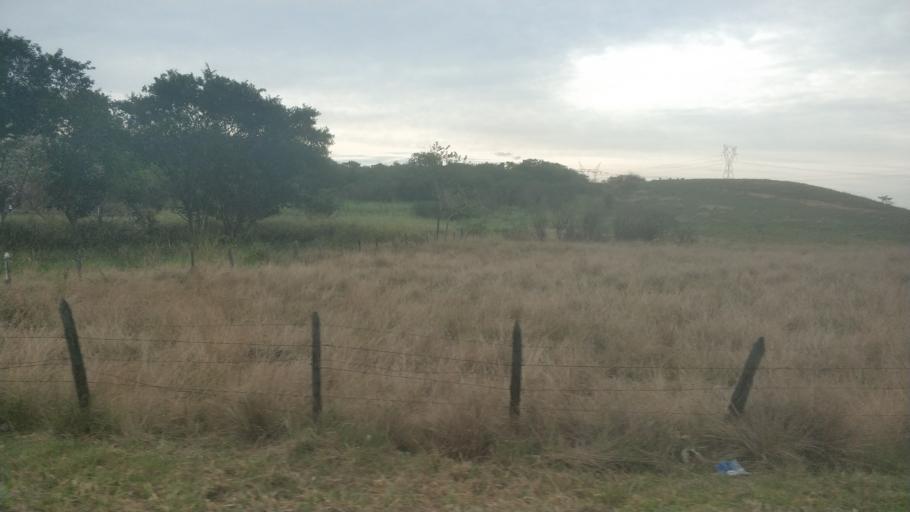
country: BR
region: Rio de Janeiro
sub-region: Seropedica
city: Seropedica
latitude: -22.7796
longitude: -43.6610
